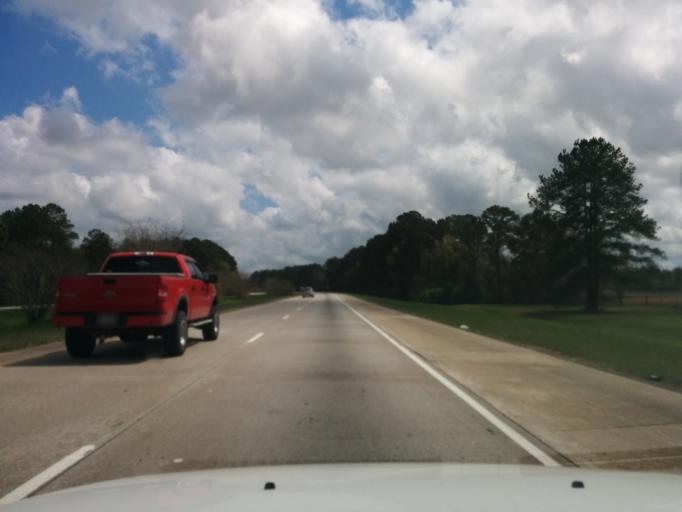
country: US
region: Georgia
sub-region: Bulloch County
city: Brooklet
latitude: 32.2598
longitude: -81.7270
